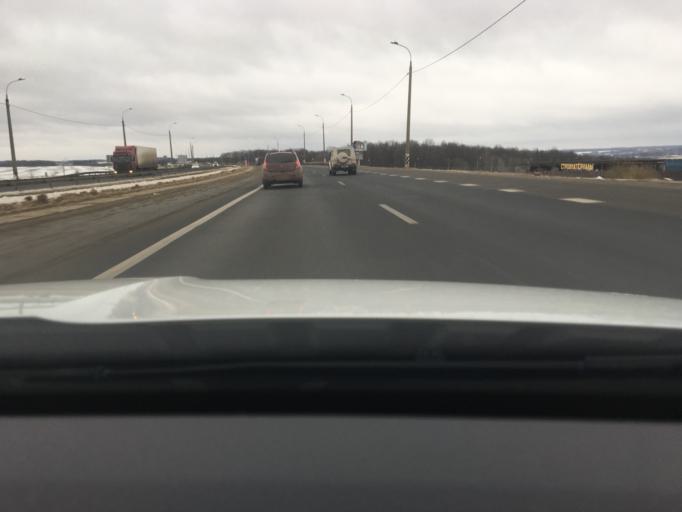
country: RU
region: Moskovskaya
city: Serpukhov
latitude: 54.8352
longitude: 37.4615
